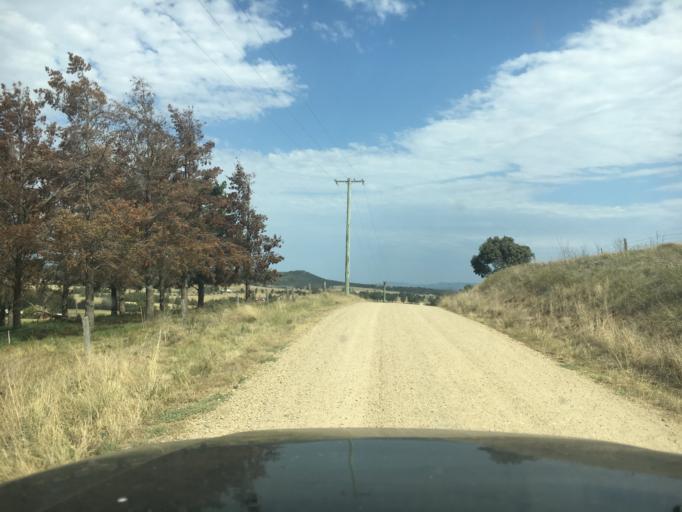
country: AU
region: New South Wales
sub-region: Cessnock
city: Branxton
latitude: -32.5047
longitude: 151.3161
